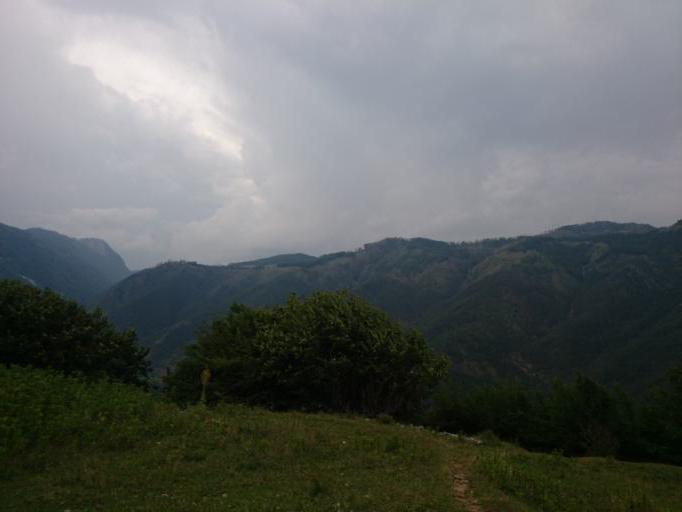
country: AL
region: Diber
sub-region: Rrethi i Dibres
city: Fushe-Lure
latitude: 41.7657
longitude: 20.2261
